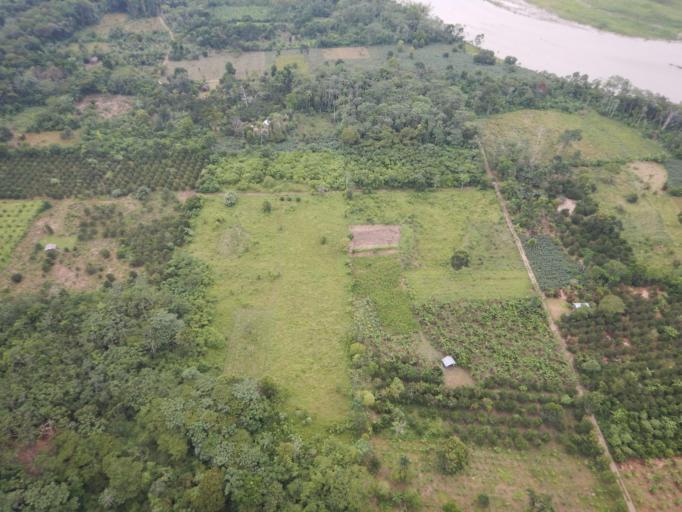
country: BO
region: Cochabamba
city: Chimore
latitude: -17.1213
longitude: -64.8014
